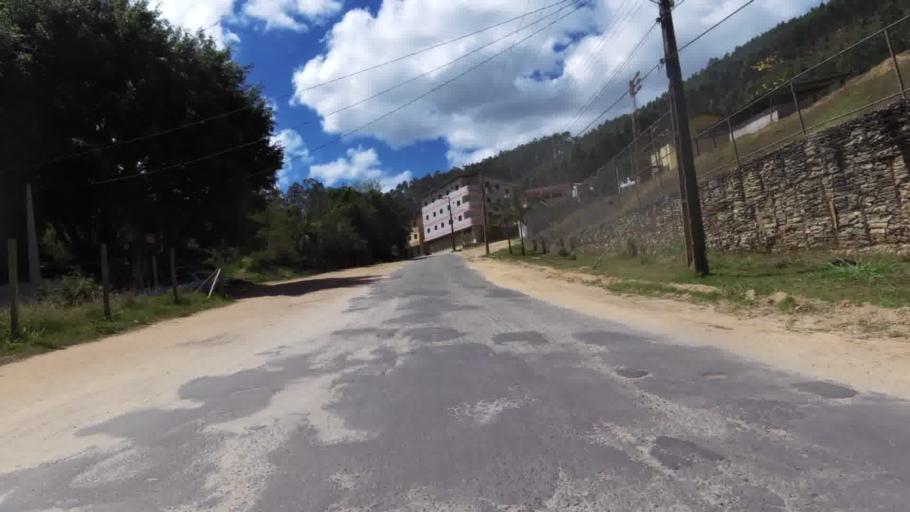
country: BR
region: Espirito Santo
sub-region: Vargem Alta
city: Vargem Alta
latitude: -20.6730
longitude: -41.0054
